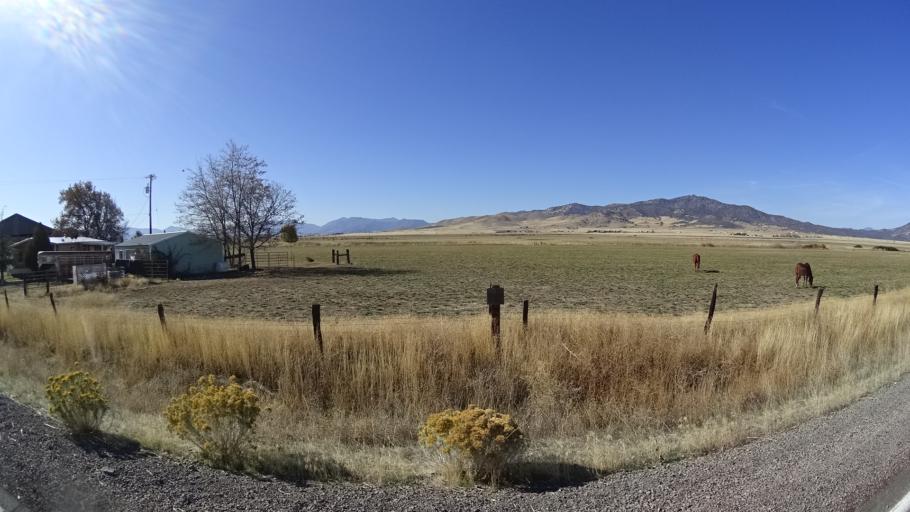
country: US
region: California
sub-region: Siskiyou County
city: Montague
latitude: 41.7780
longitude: -122.4737
